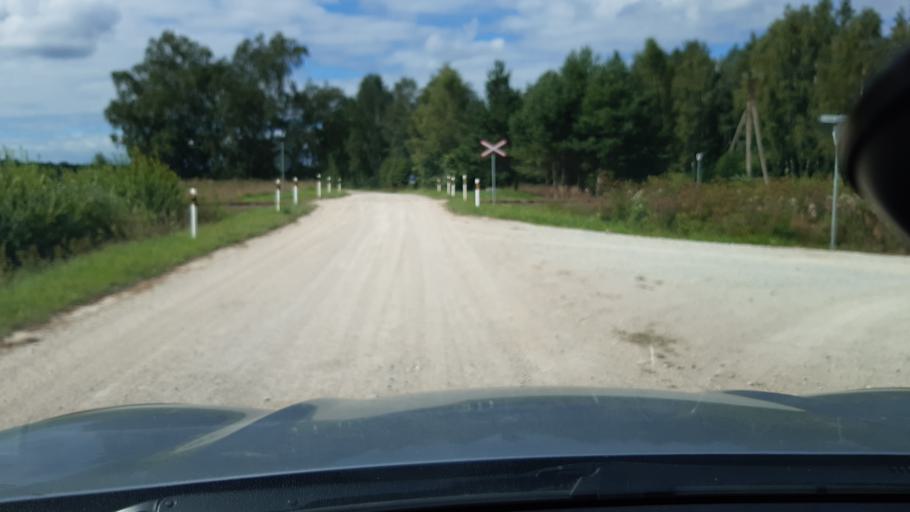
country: EE
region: Paernumaa
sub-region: Vaendra vald (alev)
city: Vandra
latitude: 58.7943
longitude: 24.9995
